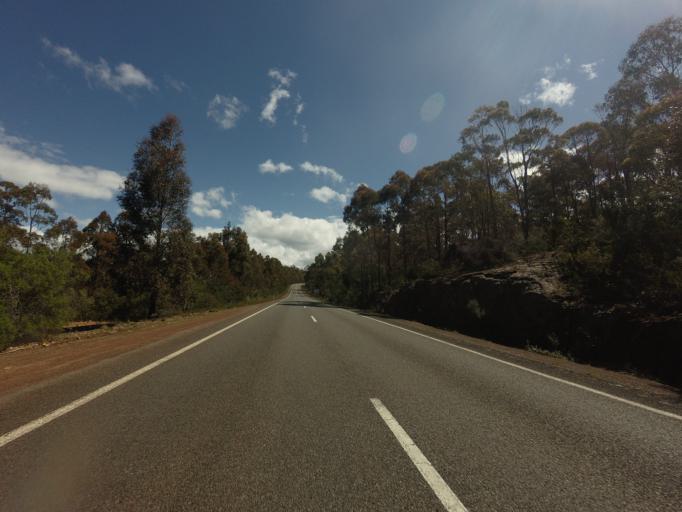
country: AU
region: Tasmania
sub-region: Northern Midlands
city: Evandale
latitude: -42.0151
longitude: 147.8603
